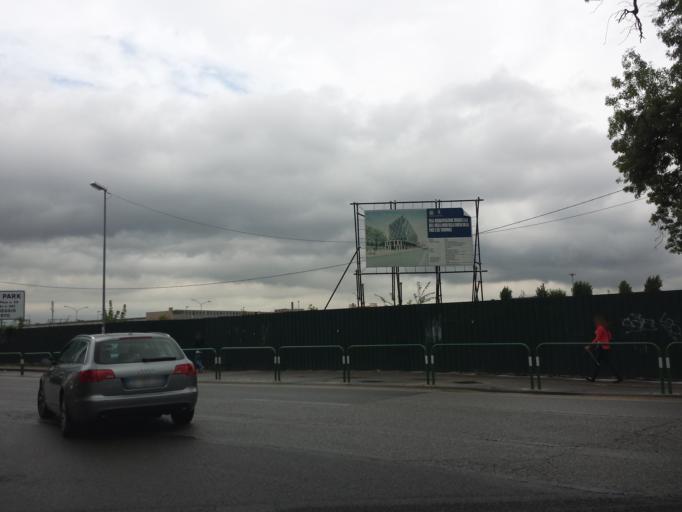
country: IT
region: Veneto
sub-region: Provincia di Padova
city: Padova
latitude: 45.4152
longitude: 11.8839
